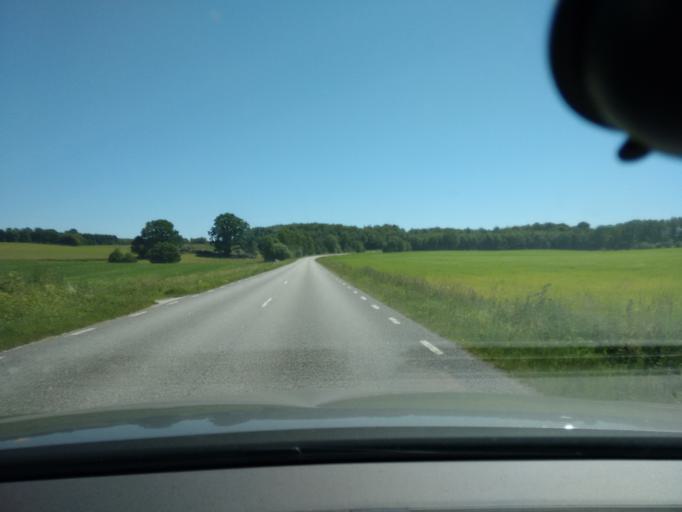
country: SE
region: Skane
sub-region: Kristianstads Kommun
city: Degeberga
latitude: 55.7797
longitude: 13.8853
